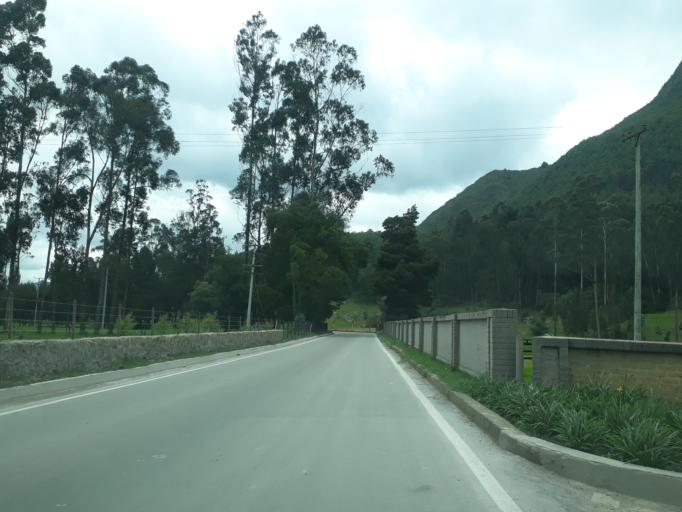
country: CO
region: Cundinamarca
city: Lenguazaque
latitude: 5.3253
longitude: -73.7396
